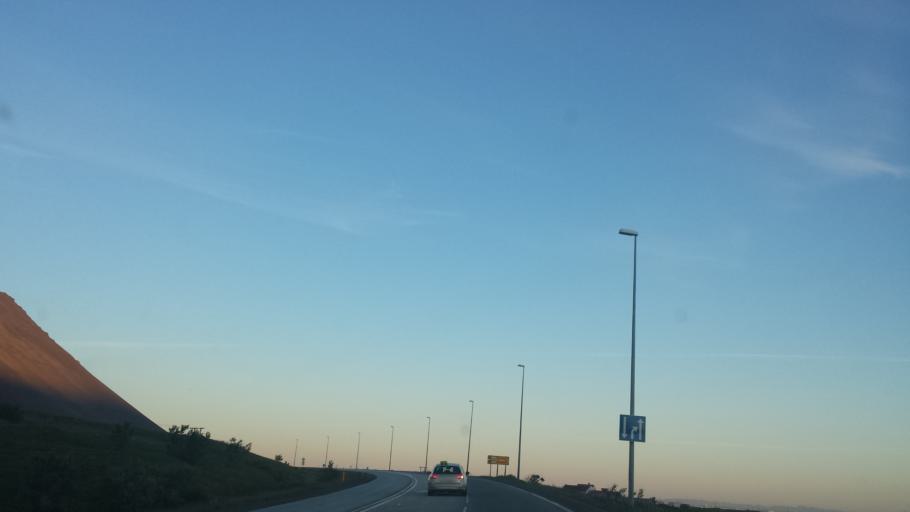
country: IS
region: Capital Region
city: Reykjavik
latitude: 64.2775
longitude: -21.8408
